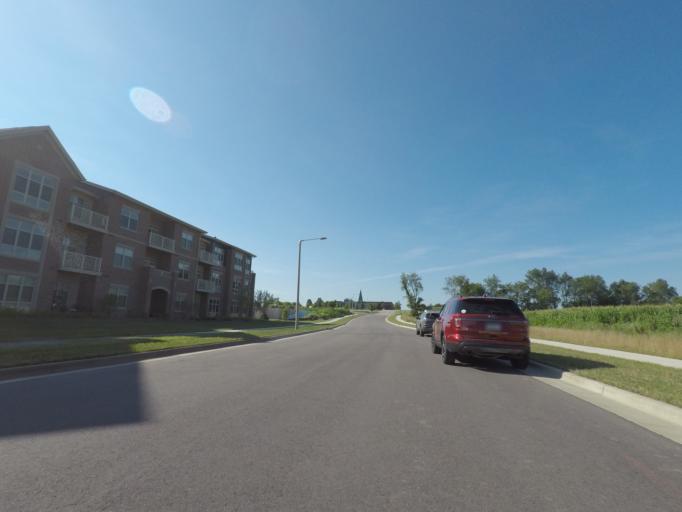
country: US
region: Wisconsin
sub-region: Dane County
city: Middleton
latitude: 43.0653
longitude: -89.5550
